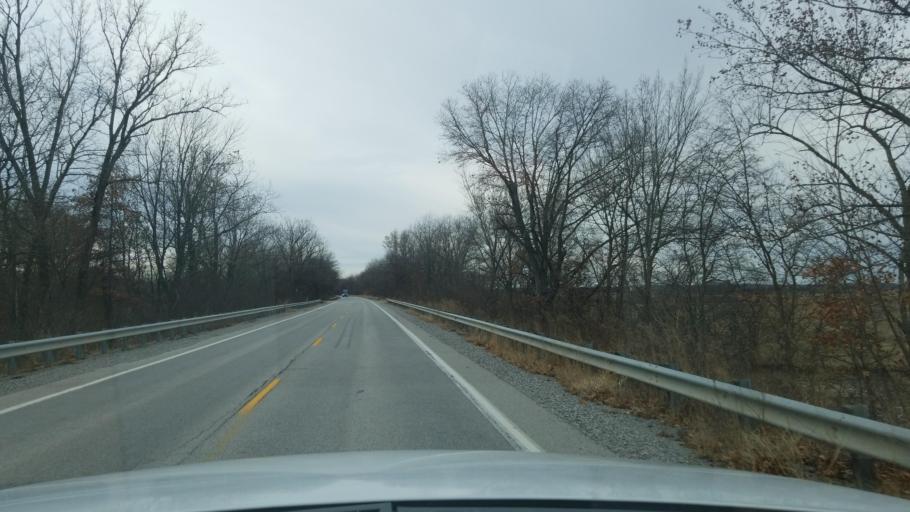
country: US
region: Illinois
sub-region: White County
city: Carmi
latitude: 37.9364
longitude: -88.0788
